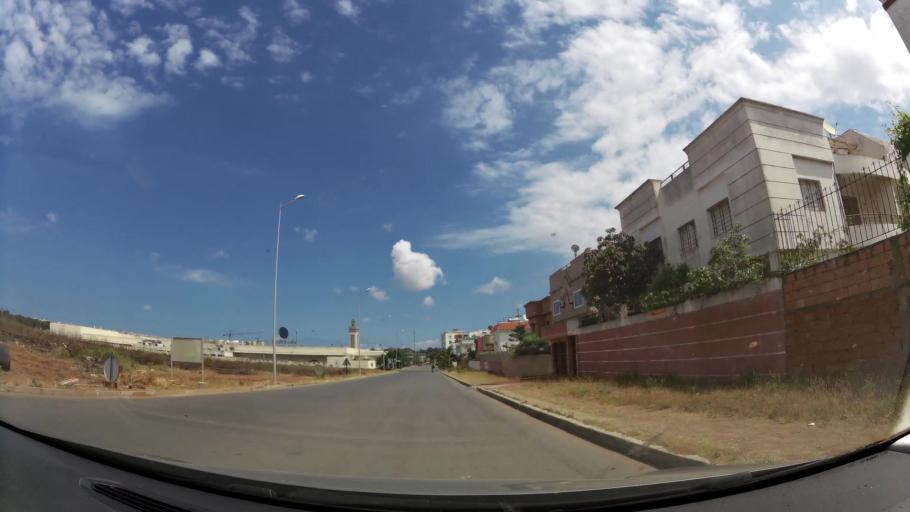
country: MA
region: Gharb-Chrarda-Beni Hssen
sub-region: Kenitra Province
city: Kenitra
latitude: 34.2456
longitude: -6.6076
